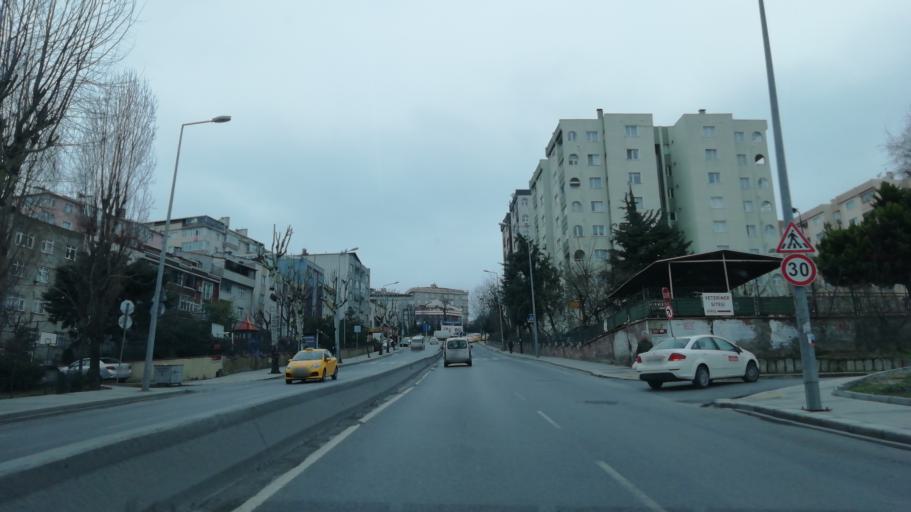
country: TR
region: Istanbul
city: Mahmutbey
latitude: 41.0089
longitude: 28.8035
